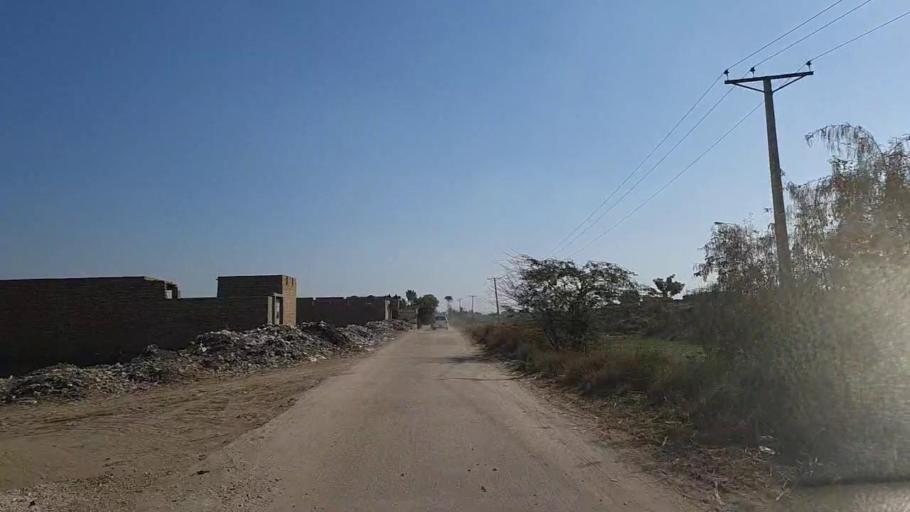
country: PK
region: Sindh
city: Nawabshah
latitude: 26.2410
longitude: 68.4236
